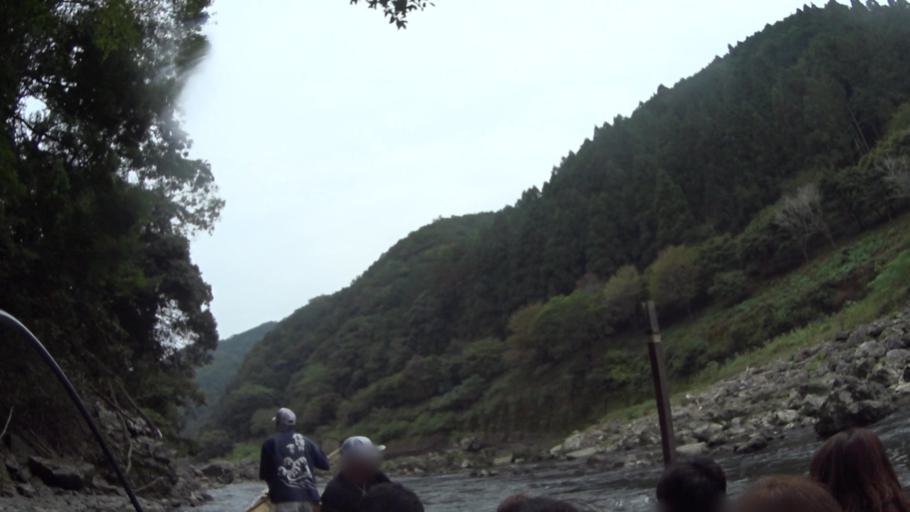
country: JP
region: Kyoto
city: Kameoka
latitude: 35.0180
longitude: 135.6343
